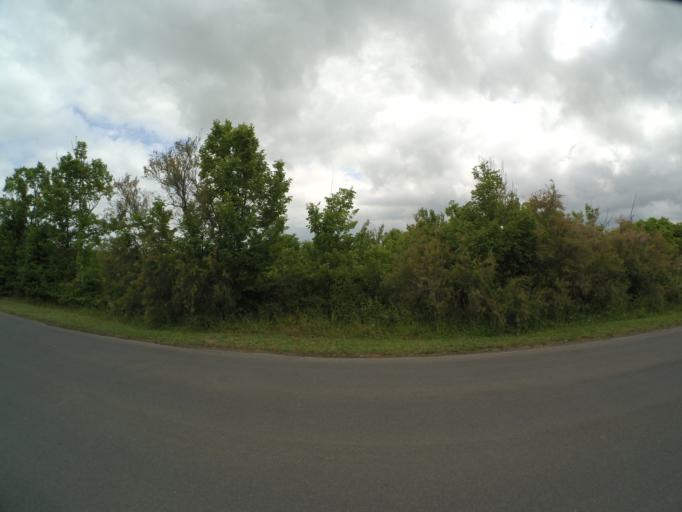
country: FR
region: Poitou-Charentes
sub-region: Departement de la Charente-Maritime
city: Saint-Laurent-de-la-Pree
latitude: 45.9810
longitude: -1.0003
